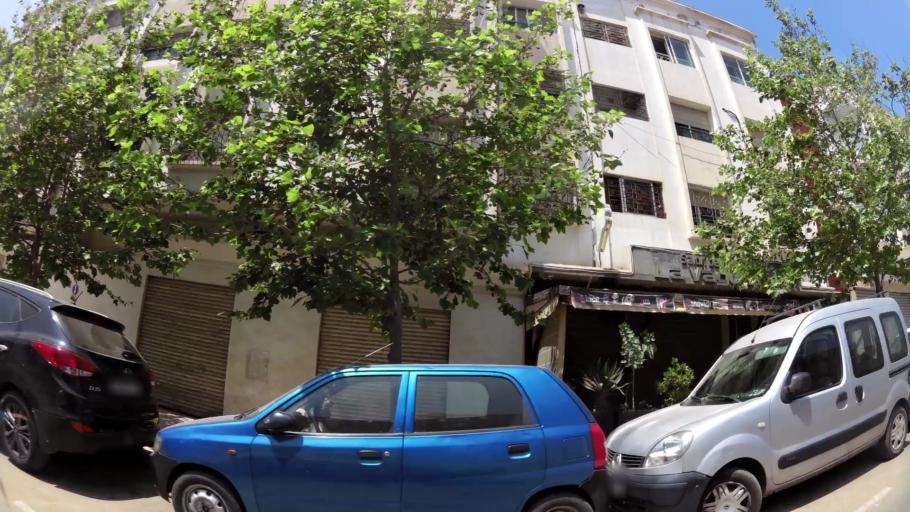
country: MA
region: Rabat-Sale-Zemmour-Zaer
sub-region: Rabat
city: Rabat
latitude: 34.0260
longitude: -6.8419
